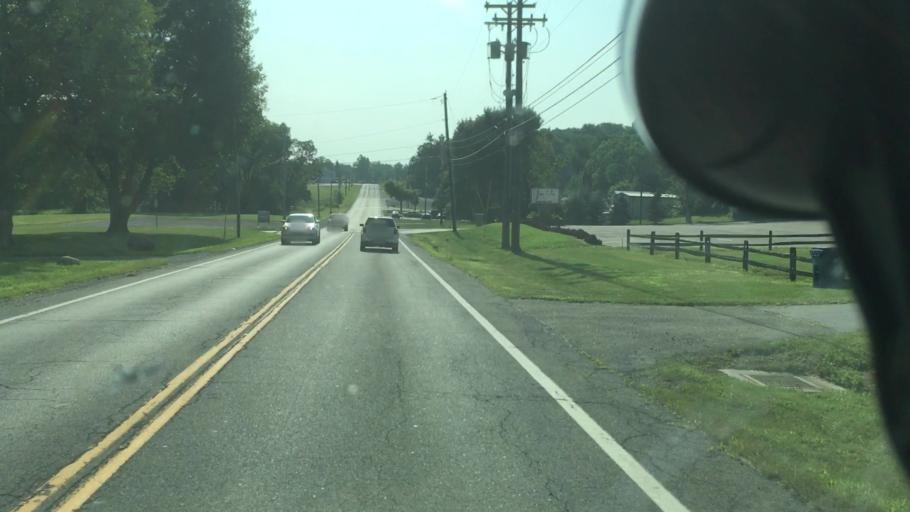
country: US
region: Ohio
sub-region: Mahoning County
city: Lowellville
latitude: 41.0239
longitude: -80.5281
